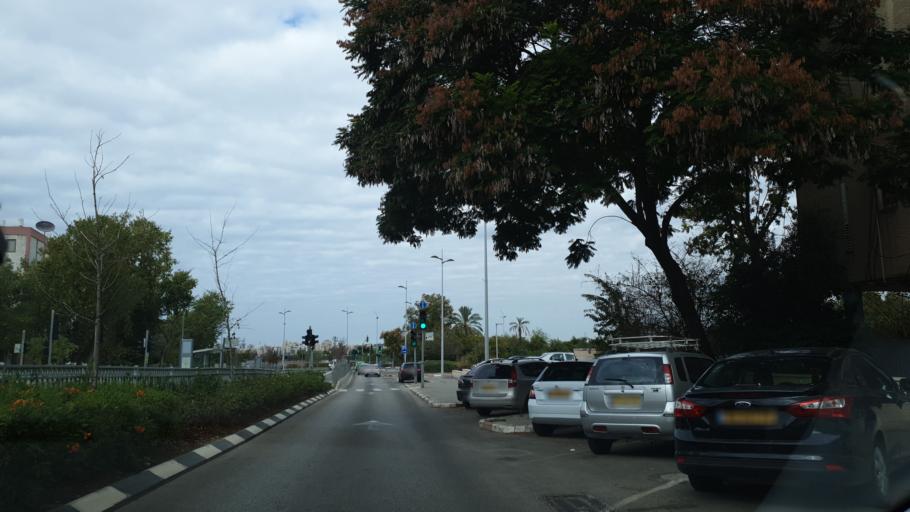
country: IL
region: Haifa
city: Qiryat Ata
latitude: 32.8172
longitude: 35.1134
